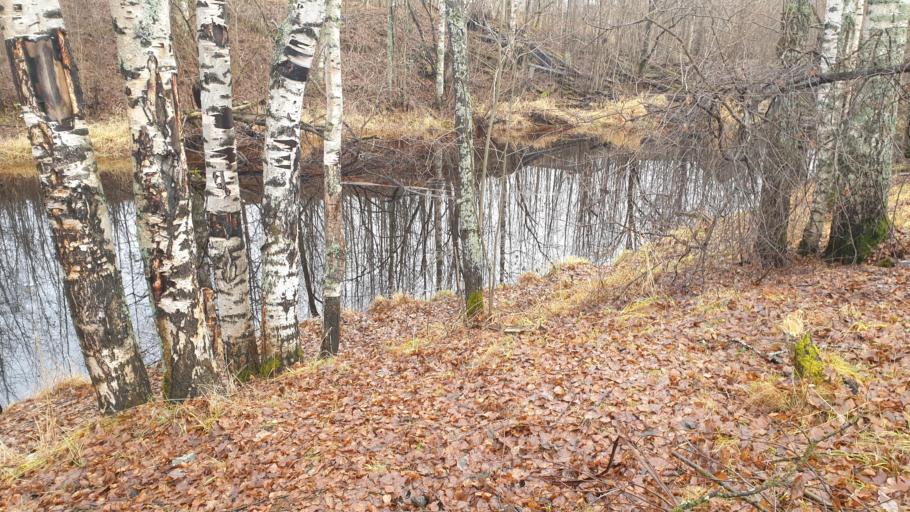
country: RU
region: Kirov
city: Kirs
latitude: 59.3327
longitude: 52.2372
